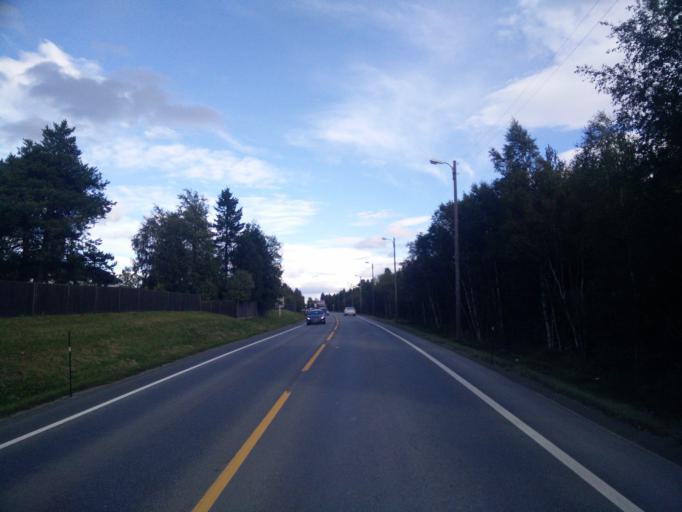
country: NO
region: Sor-Trondelag
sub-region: Trondheim
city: Trondheim
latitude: 63.3440
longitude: 10.3674
